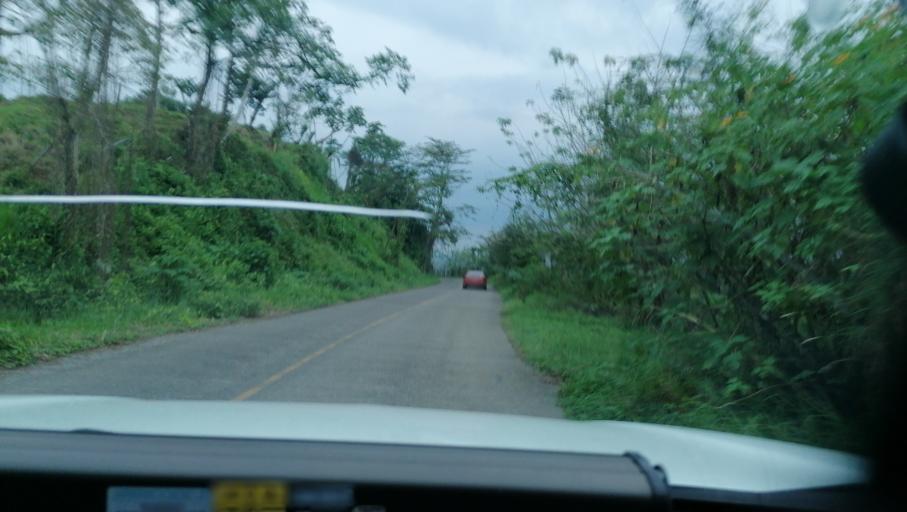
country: MX
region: Chiapas
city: Ixtacomitan
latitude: 17.3968
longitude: -93.0983
